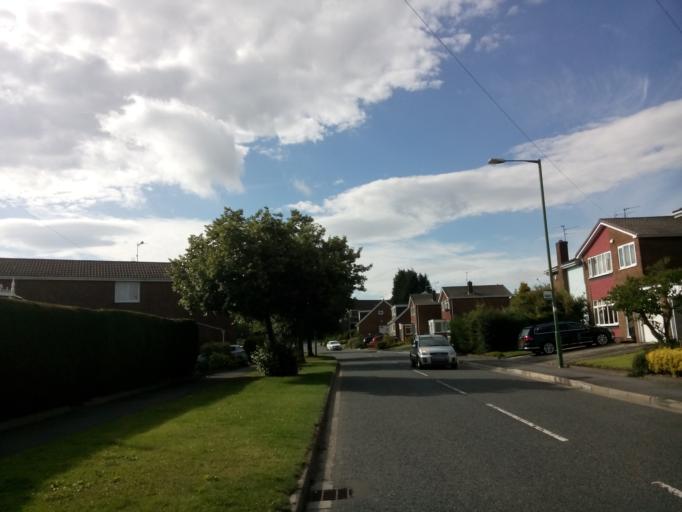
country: GB
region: England
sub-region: County Durham
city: Durham
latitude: 54.8049
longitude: -1.5675
